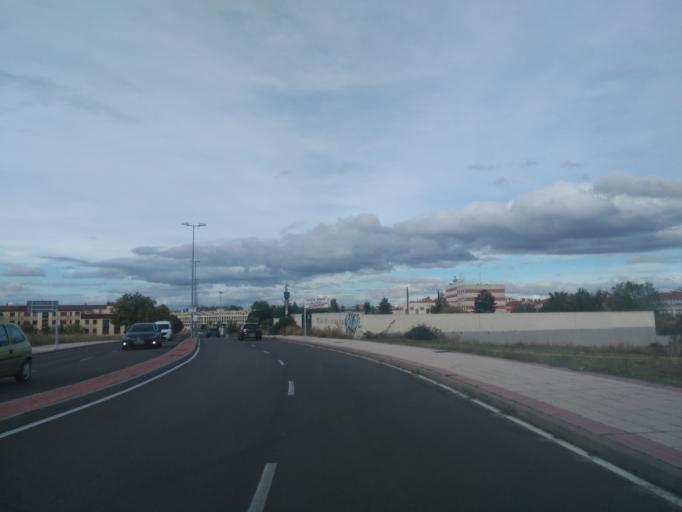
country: ES
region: Castille and Leon
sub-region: Provincia de Salamanca
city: Santa Marta de Tormes
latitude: 40.9473
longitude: -5.6418
